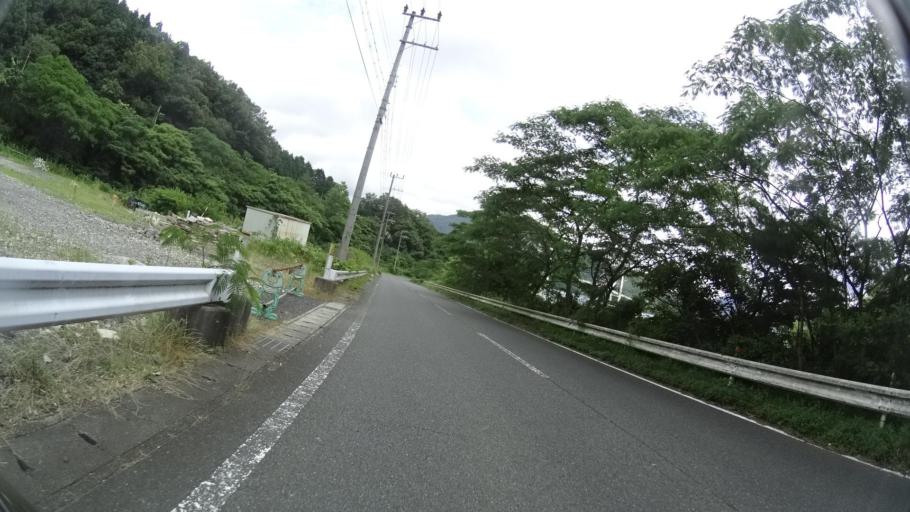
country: JP
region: Kyoto
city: Maizuru
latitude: 35.5103
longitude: 135.3817
